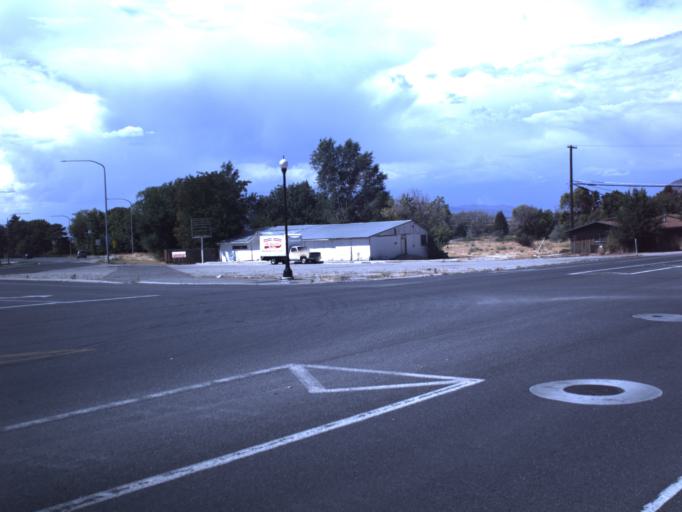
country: US
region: Utah
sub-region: Box Elder County
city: Brigham City
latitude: 41.5281
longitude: -112.0154
